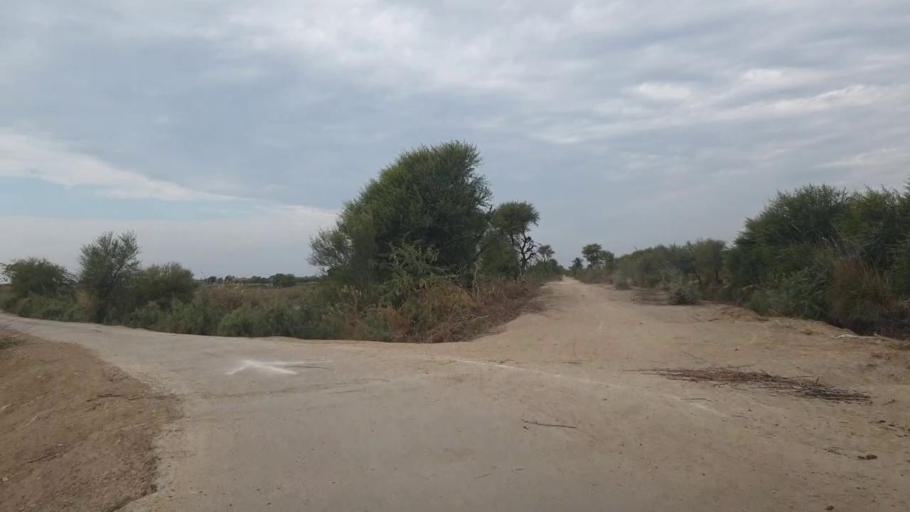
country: PK
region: Sindh
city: Jhol
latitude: 25.9979
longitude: 68.8885
